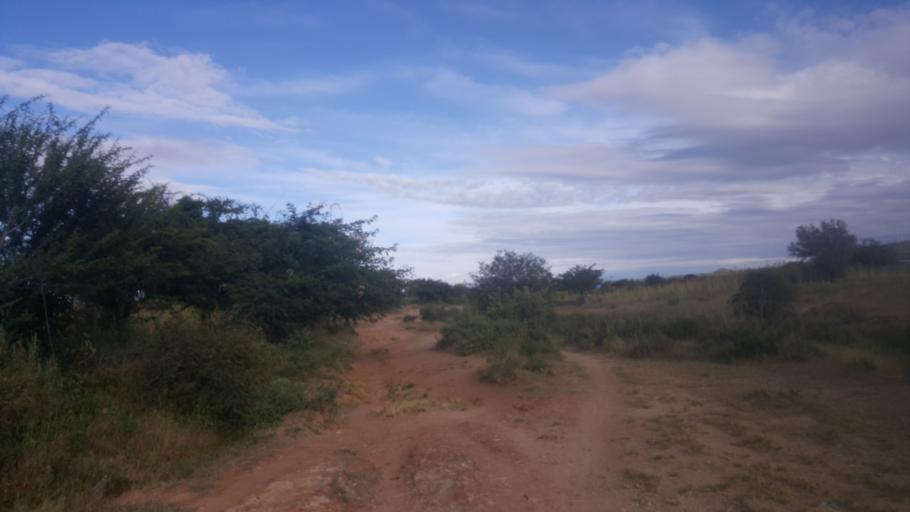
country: TZ
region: Dodoma
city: Dodoma
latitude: -6.0977
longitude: 35.5326
